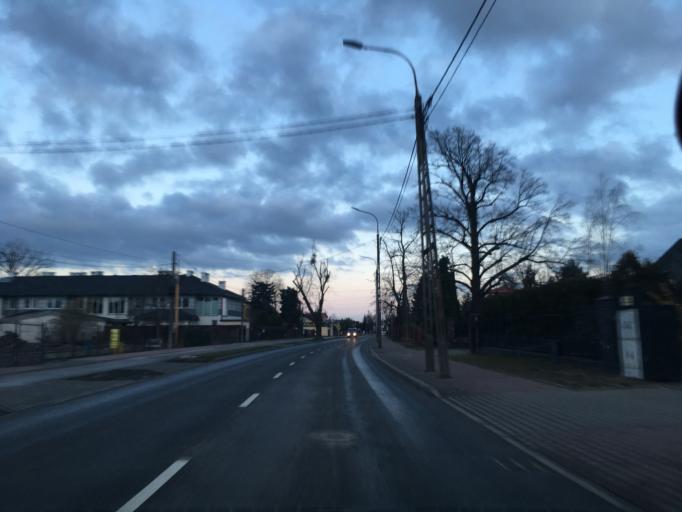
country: PL
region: Masovian Voivodeship
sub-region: Powiat grodziski
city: Grodzisk Mazowiecki
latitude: 52.1009
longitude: 20.6416
